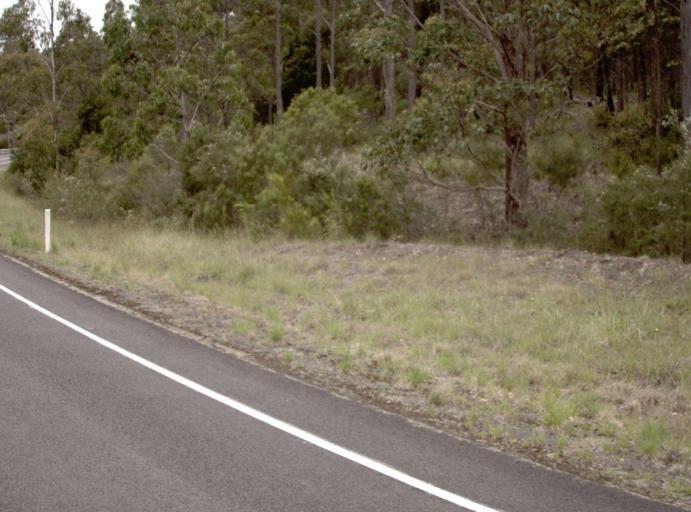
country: AU
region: New South Wales
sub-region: Bombala
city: Bombala
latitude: -37.2479
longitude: 149.2538
